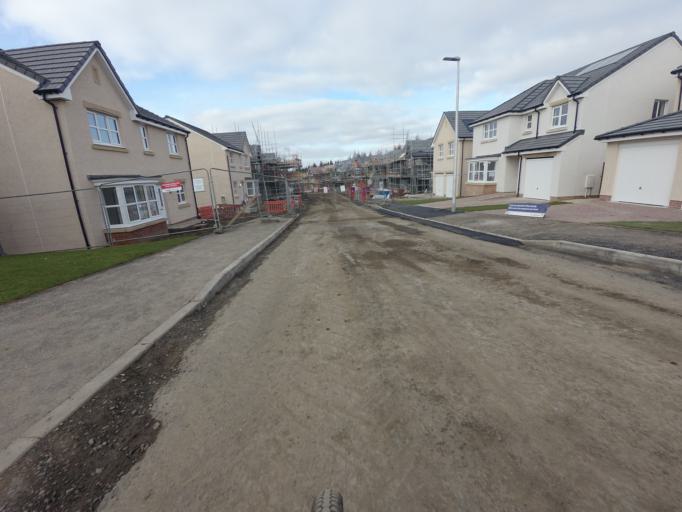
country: GB
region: Scotland
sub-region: West Lothian
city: West Calder
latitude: 55.8692
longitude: -3.5382
